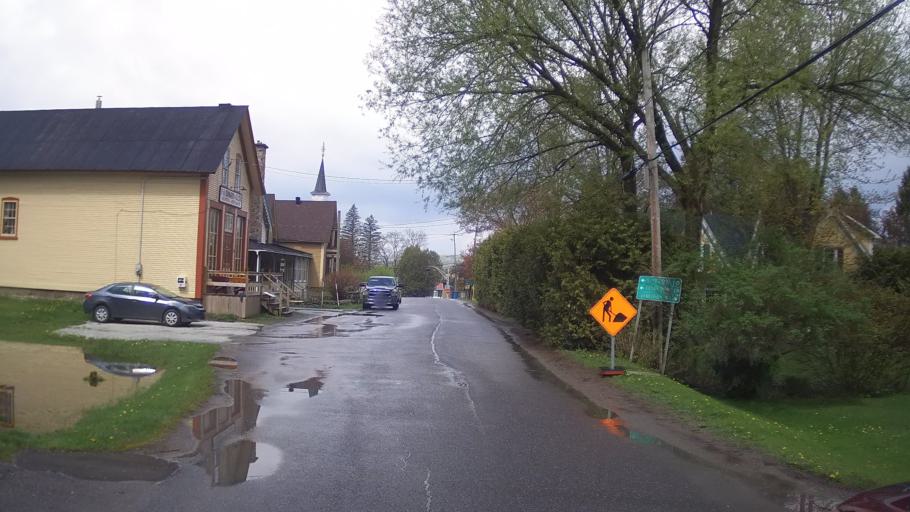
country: CA
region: Quebec
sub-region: Monteregie
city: Sutton
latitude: 45.1759
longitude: -72.6603
